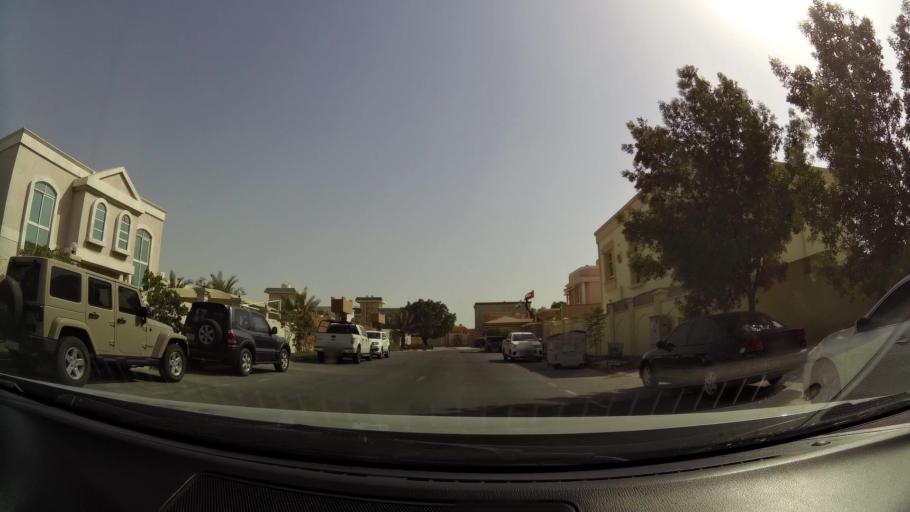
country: AE
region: Dubai
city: Dubai
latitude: 25.1661
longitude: 55.2473
